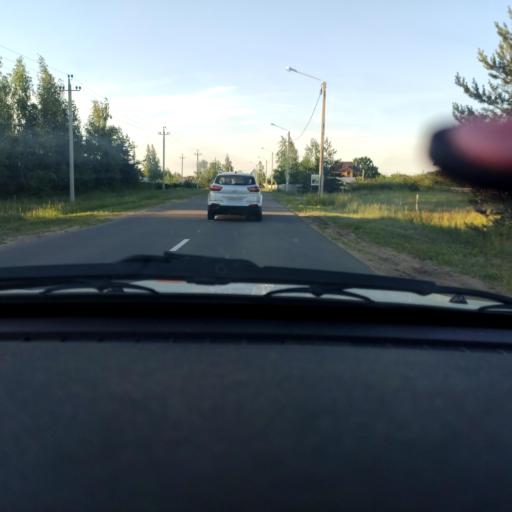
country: RU
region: Voronezj
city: Ramon'
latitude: 51.8900
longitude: 39.2525
